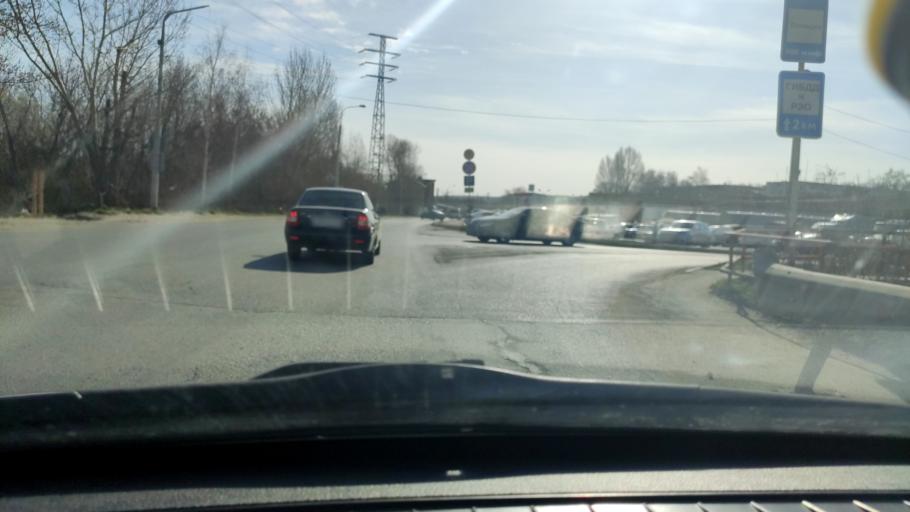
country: RU
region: Samara
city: Zhigulevsk
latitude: 53.4084
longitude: 49.4829
